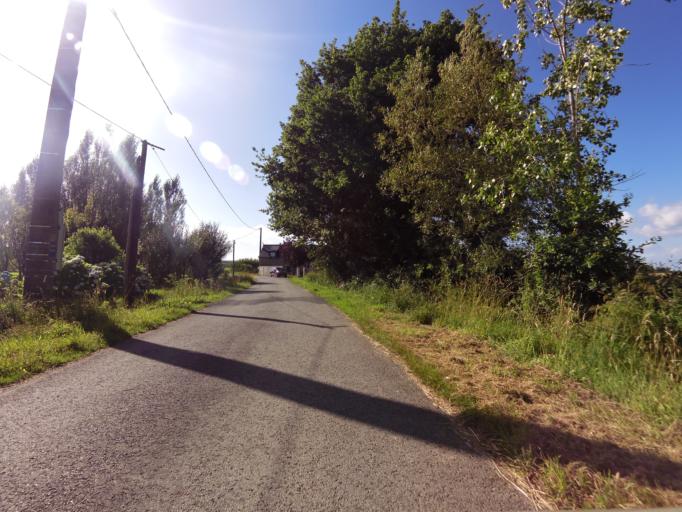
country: FR
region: Brittany
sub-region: Departement du Morbihan
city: Caden
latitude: 47.6338
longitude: -2.2617
